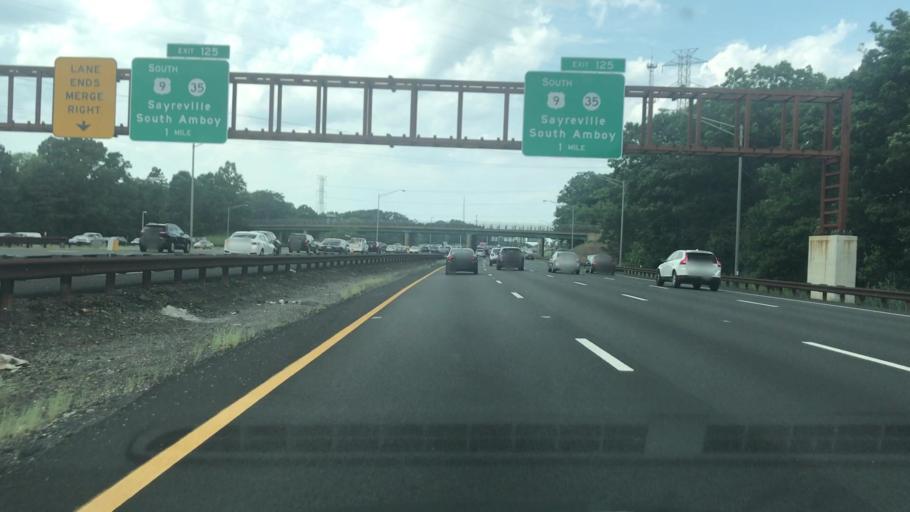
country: US
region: New Jersey
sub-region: Middlesex County
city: South Amboy
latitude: 40.4748
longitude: -74.2979
